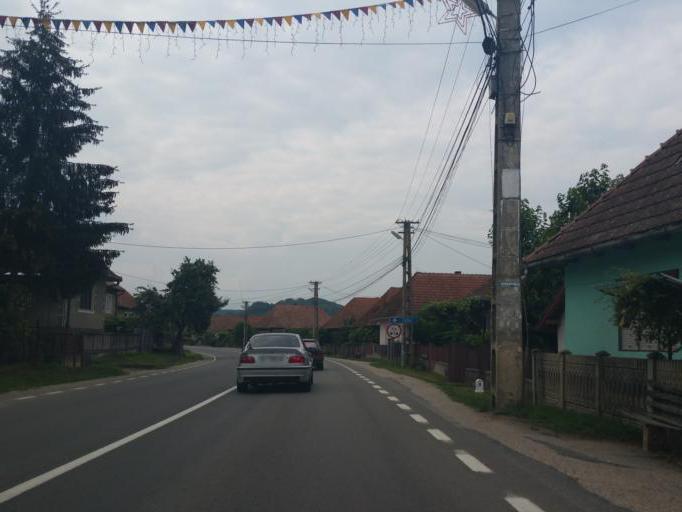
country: RO
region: Salaj
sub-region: Comuna Hida
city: Hida
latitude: 47.0378
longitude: 23.2659
